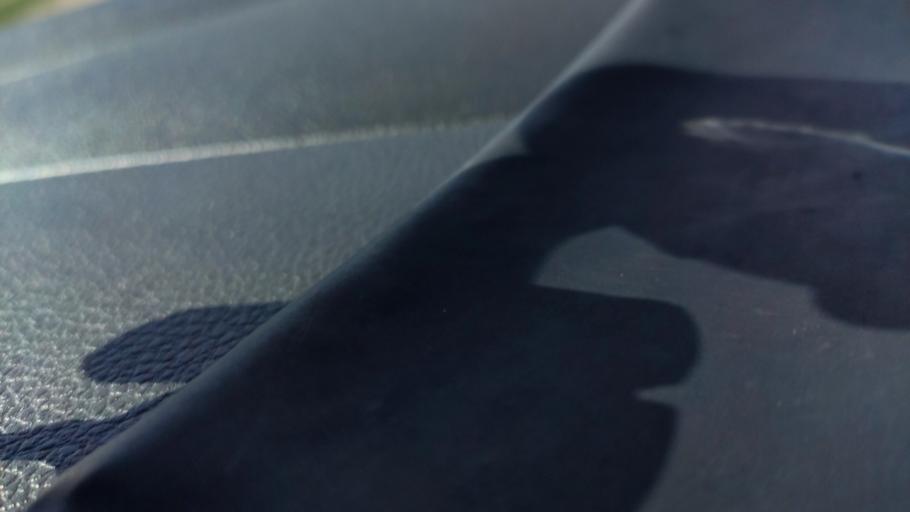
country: RU
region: Voronezj
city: Maslovka
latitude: 51.5023
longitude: 39.2995
